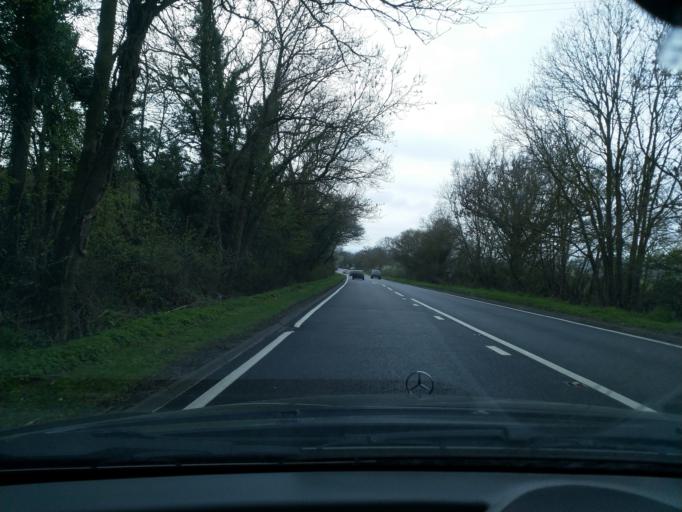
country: GB
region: England
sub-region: Warwickshire
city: Stratford-upon-Avon
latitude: 52.2279
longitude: -1.6636
